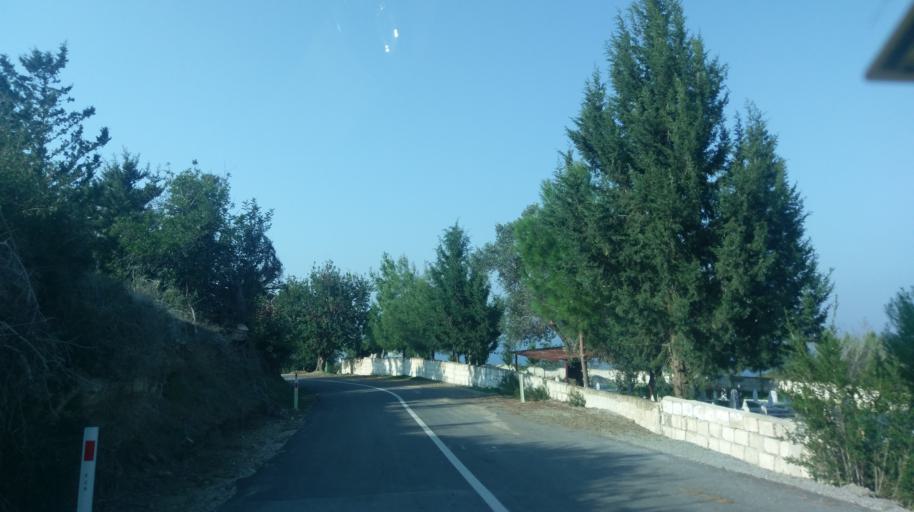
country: CY
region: Ammochostos
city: Leonarisso
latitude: 35.5353
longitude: 34.2321
